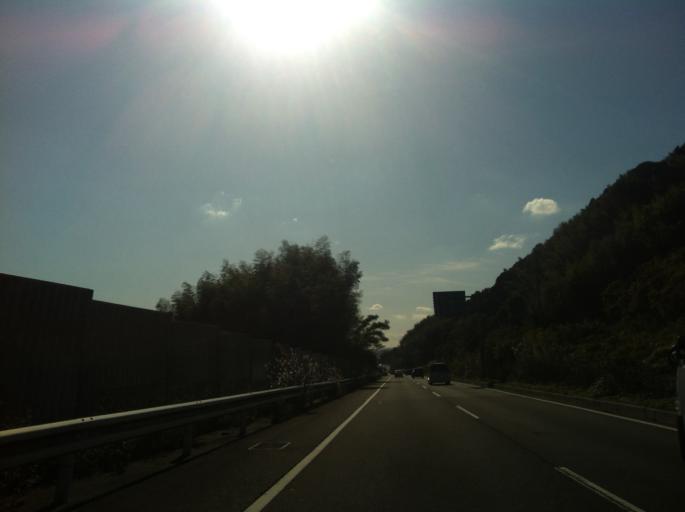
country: JP
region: Shizuoka
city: Fujieda
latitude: 34.9147
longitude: 138.2904
